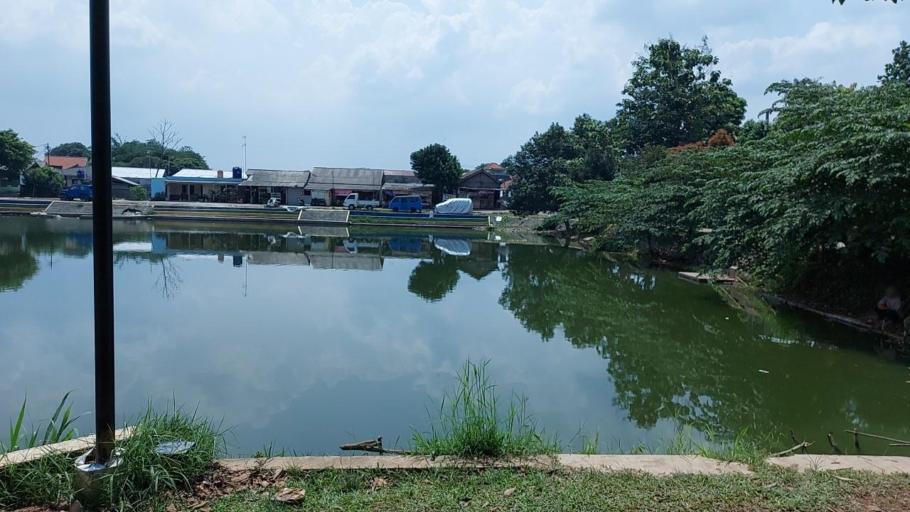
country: ID
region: West Java
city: Cibinong
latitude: -6.4711
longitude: 106.8479
